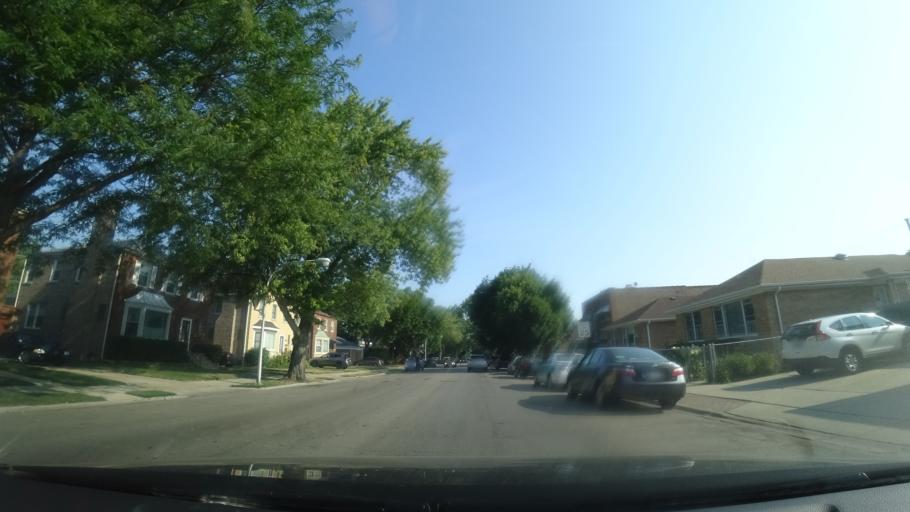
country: US
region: Illinois
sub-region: Cook County
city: Lincolnwood
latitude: 41.9796
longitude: -87.6991
